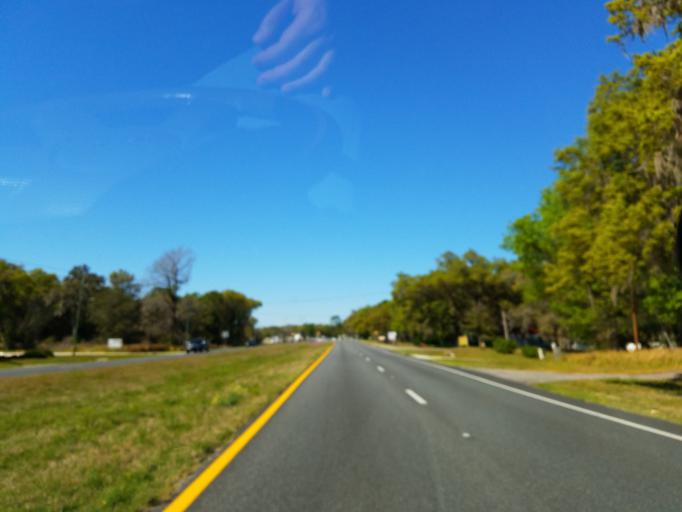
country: US
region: Florida
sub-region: Marion County
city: Belleview
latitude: 29.0506
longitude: -82.0463
